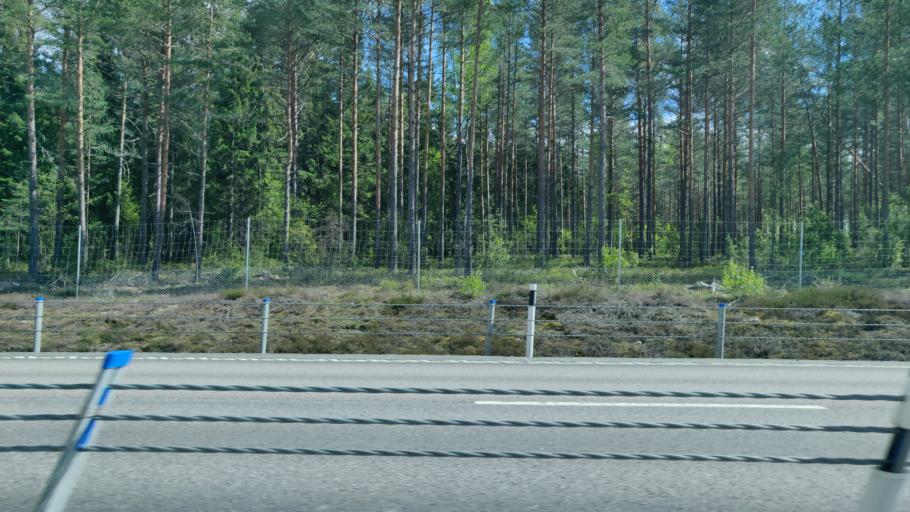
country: SE
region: Vaermland
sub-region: Karlstads Kommun
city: Karlstad
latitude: 59.4254
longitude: 13.5347
